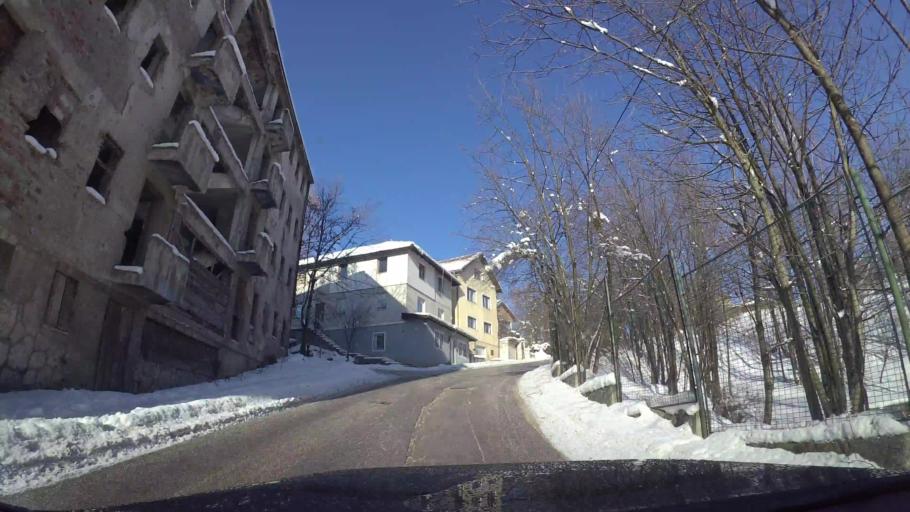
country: BA
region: Federation of Bosnia and Herzegovina
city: Kobilja Glava
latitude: 43.8778
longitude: 18.4104
